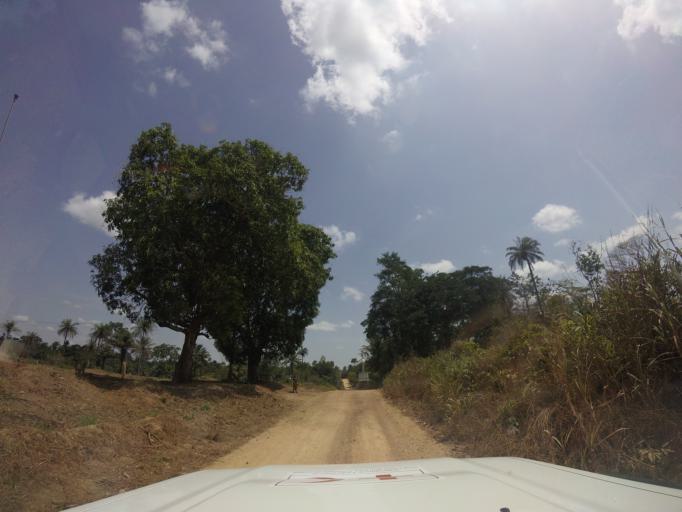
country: SL
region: Southern Province
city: Zimmi
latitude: 7.0581
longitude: -11.2768
